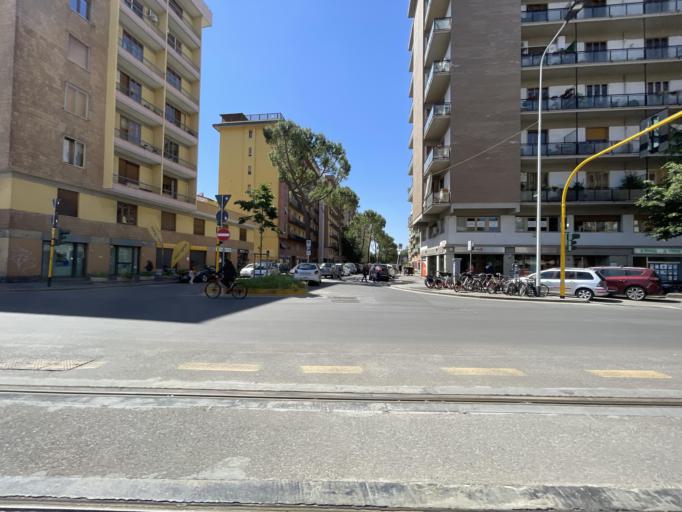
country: IT
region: Tuscany
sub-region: Province of Florence
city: Florence
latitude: 43.7934
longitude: 11.2203
